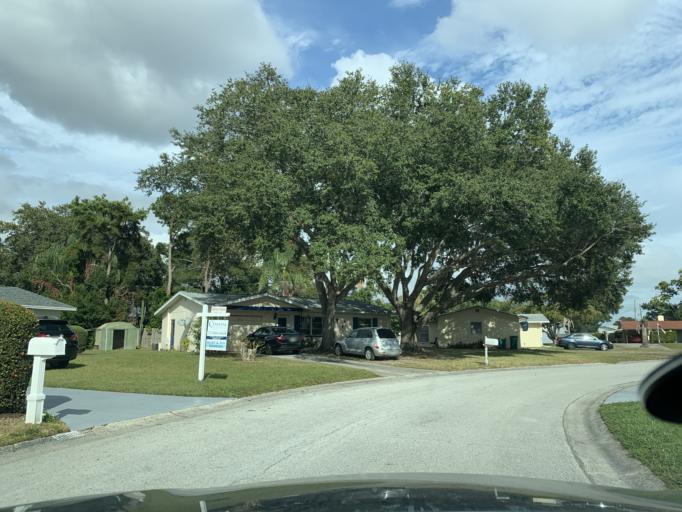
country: US
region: Florida
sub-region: Pinellas County
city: Ridgecrest
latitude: 27.8792
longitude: -82.7907
